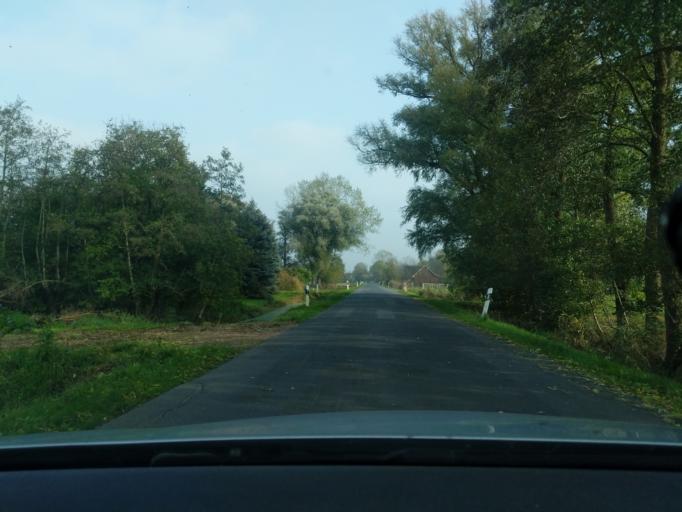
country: DE
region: Lower Saxony
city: Neuenkirchen
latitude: 53.7370
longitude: 8.8734
